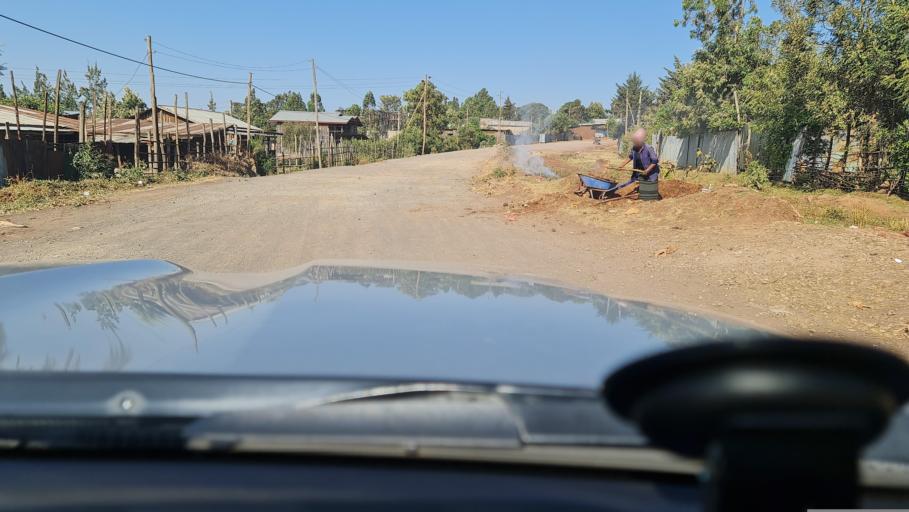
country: ET
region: Oromiya
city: Waliso
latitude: 8.6051
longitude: 37.9264
